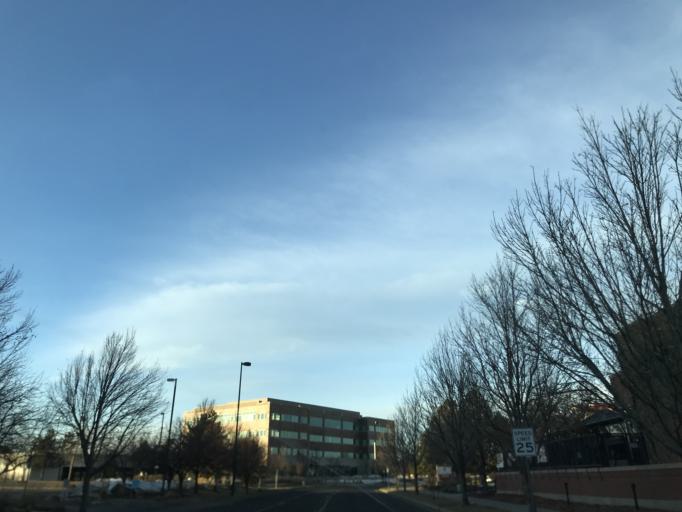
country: US
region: Colorado
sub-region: Arapahoe County
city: Glendale
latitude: 39.7189
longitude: -104.9008
